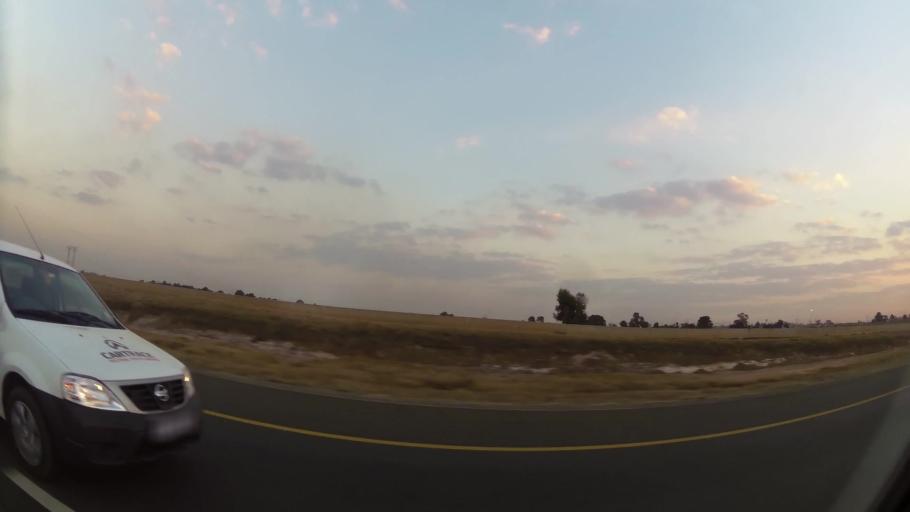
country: ZA
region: Gauteng
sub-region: Ekurhuleni Metropolitan Municipality
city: Springs
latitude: -26.2827
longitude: 28.4177
